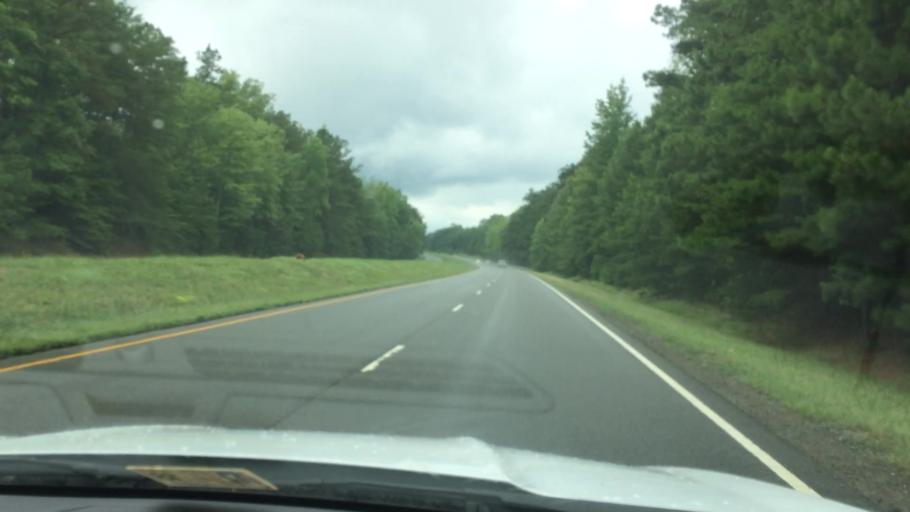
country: US
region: Virginia
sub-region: New Kent County
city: New Kent
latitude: 37.4898
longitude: -76.9040
